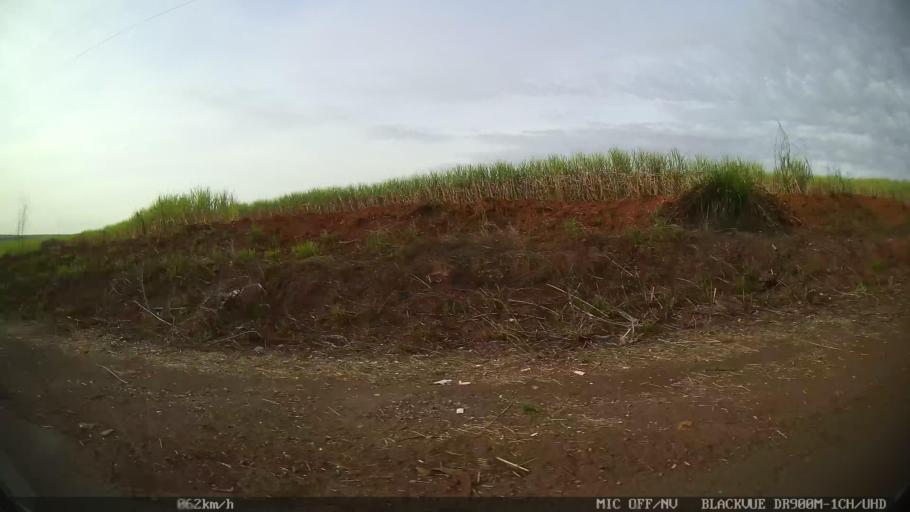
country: BR
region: Sao Paulo
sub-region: Piracicaba
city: Piracicaba
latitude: -22.7090
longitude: -47.5809
